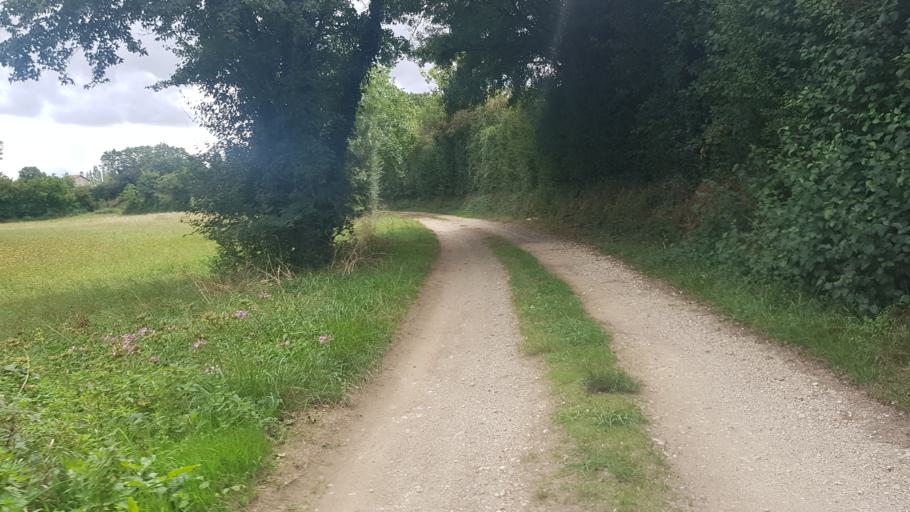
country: FR
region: Poitou-Charentes
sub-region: Departement des Deux-Sevres
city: Vouille
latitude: 46.3127
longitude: -0.3425
